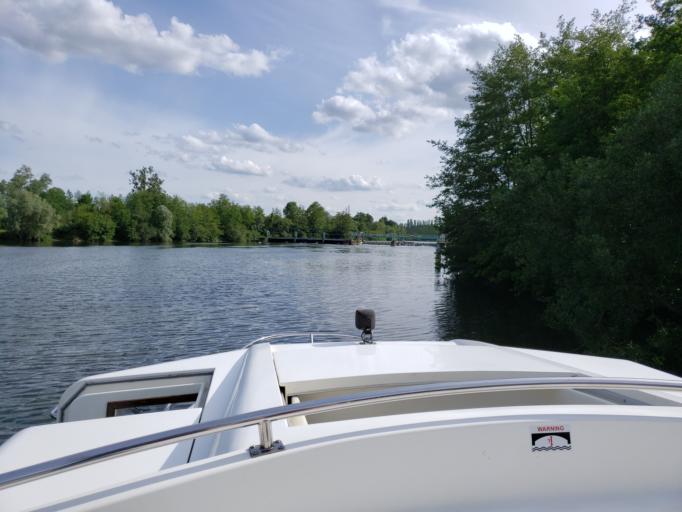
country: FR
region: Bourgogne
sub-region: Departement de l'Yonne
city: Migennes
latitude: 47.9513
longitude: 3.5072
